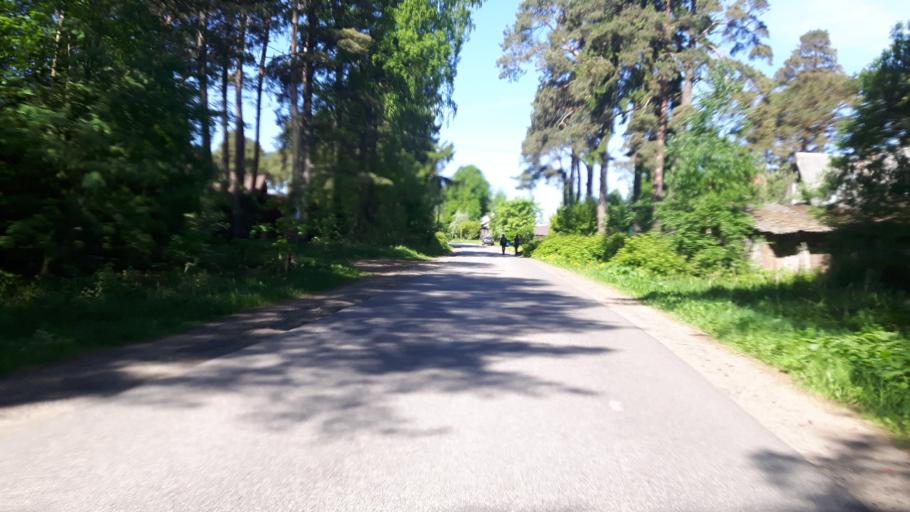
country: RU
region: Leningrad
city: Lebyazh'ye
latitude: 59.9656
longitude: 29.4049
